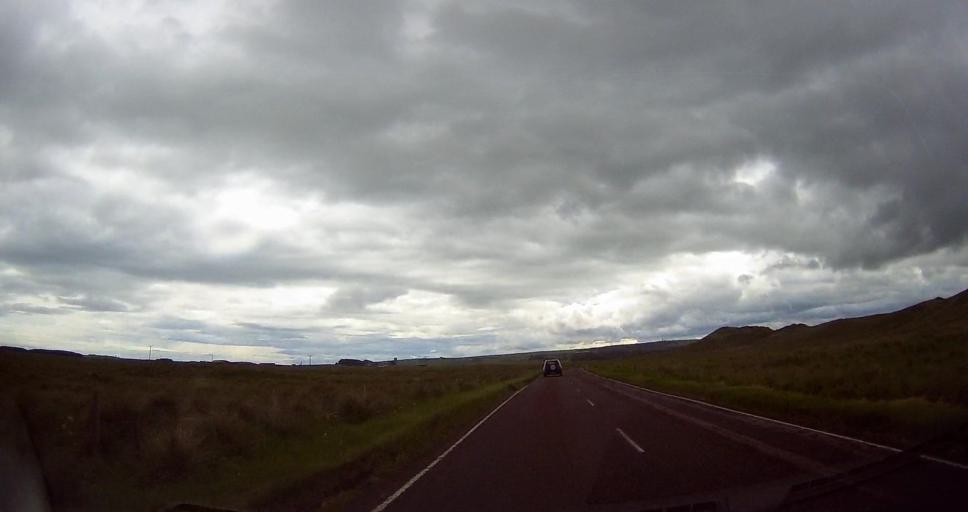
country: GB
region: Scotland
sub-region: Highland
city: Thurso
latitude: 58.5991
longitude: -3.3519
